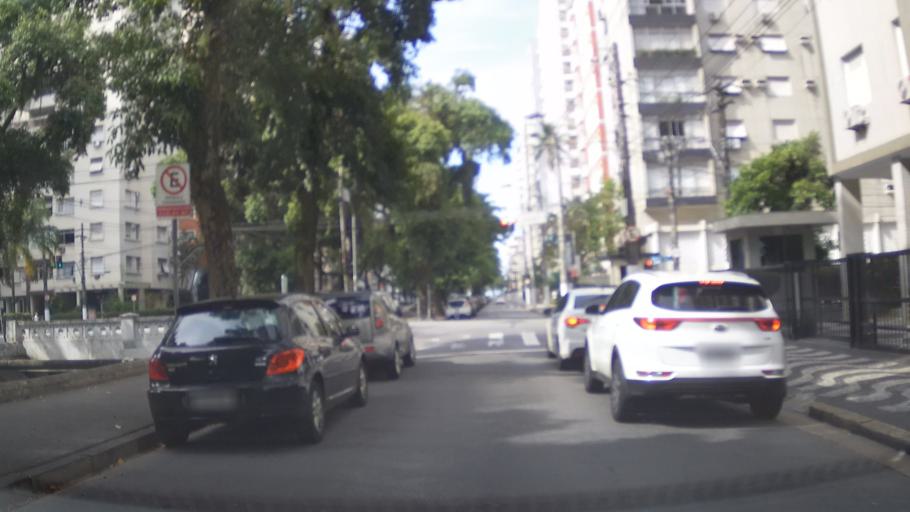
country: BR
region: Sao Paulo
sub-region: Santos
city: Santos
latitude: -23.9675
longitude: -46.3290
